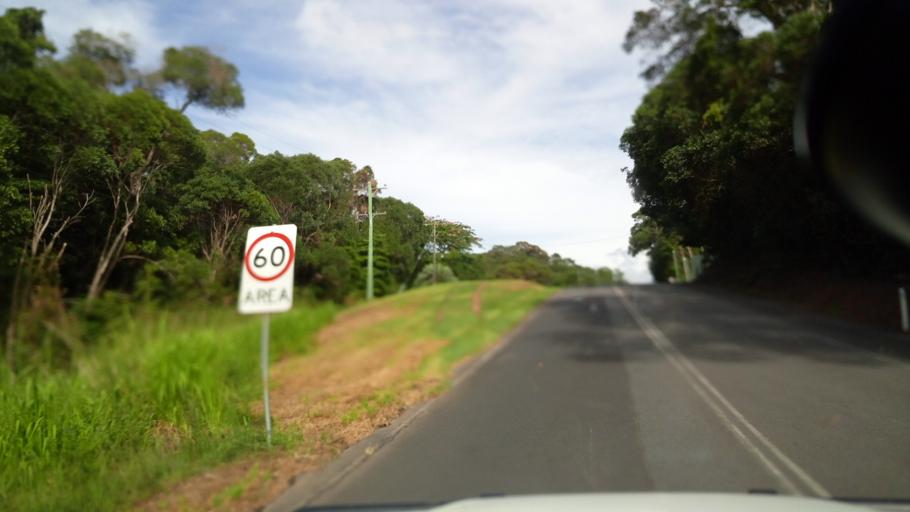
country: AU
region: Queensland
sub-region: Tablelands
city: Kuranda
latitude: -16.8223
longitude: 145.6247
